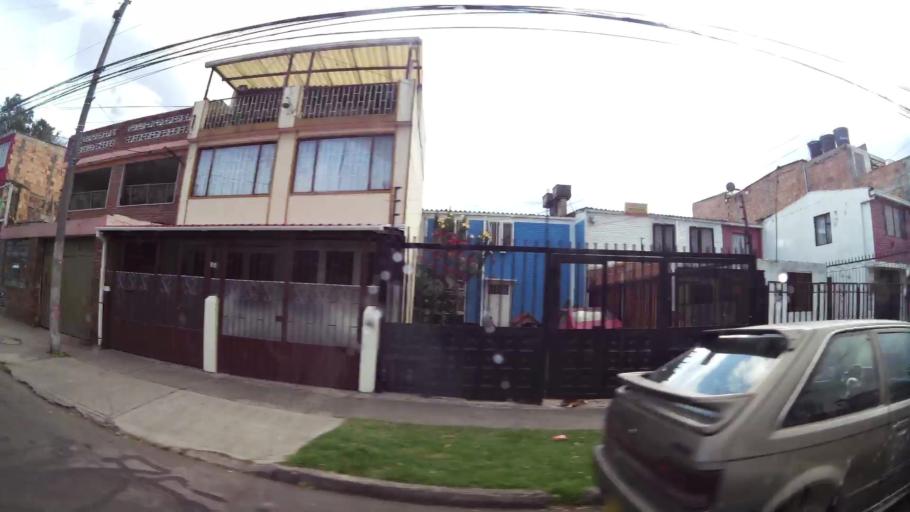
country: CO
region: Bogota D.C.
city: Bogota
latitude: 4.5979
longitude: -74.1161
